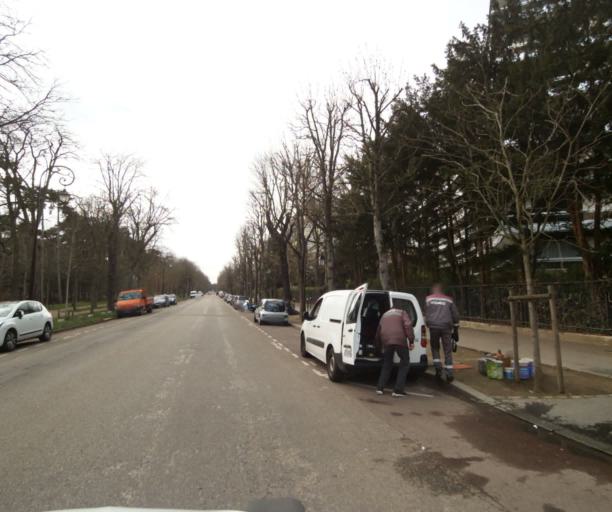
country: FR
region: Ile-de-France
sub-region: Departement des Hauts-de-Seine
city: Neuilly-sur-Seine
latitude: 48.8792
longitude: 2.2577
